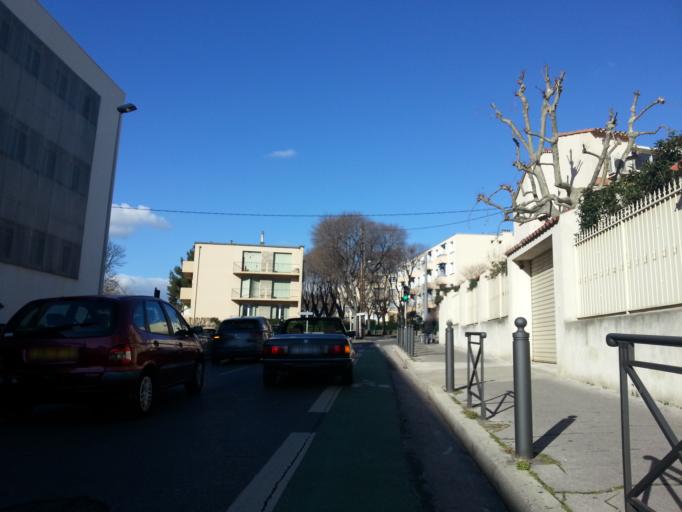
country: FR
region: Provence-Alpes-Cote d'Azur
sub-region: Departement des Bouches-du-Rhone
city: Marseille 13
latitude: 43.3054
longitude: 5.4185
